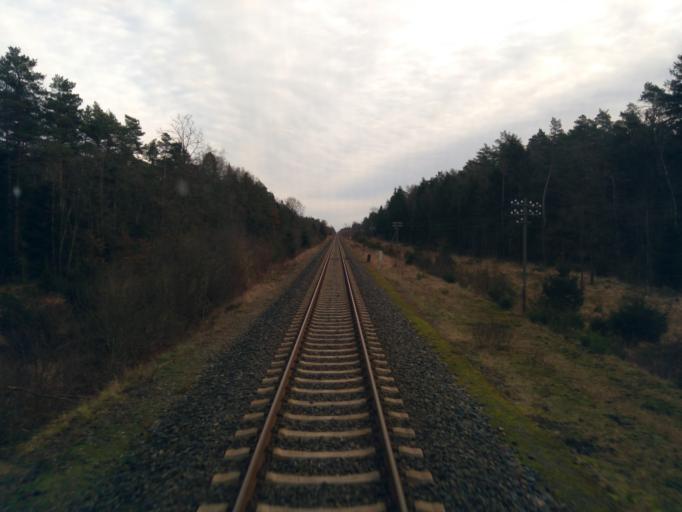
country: DE
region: Lower Saxony
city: Munster
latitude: 52.9910
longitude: 10.1383
